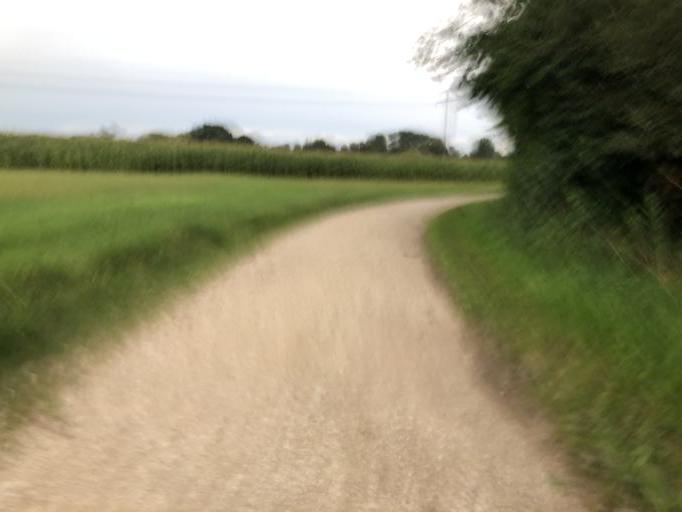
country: DE
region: Bavaria
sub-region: Regierungsbezirk Mittelfranken
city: Erlangen
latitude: 49.6014
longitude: 10.9905
